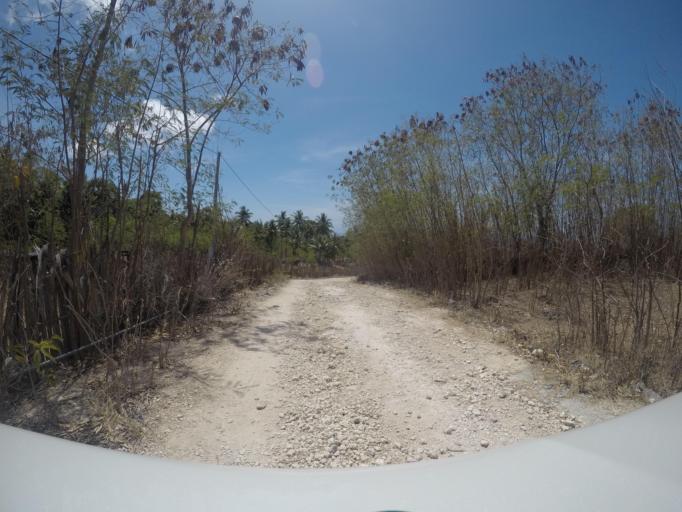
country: TL
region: Baucau
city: Baucau
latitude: -8.4460
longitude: 126.4374
